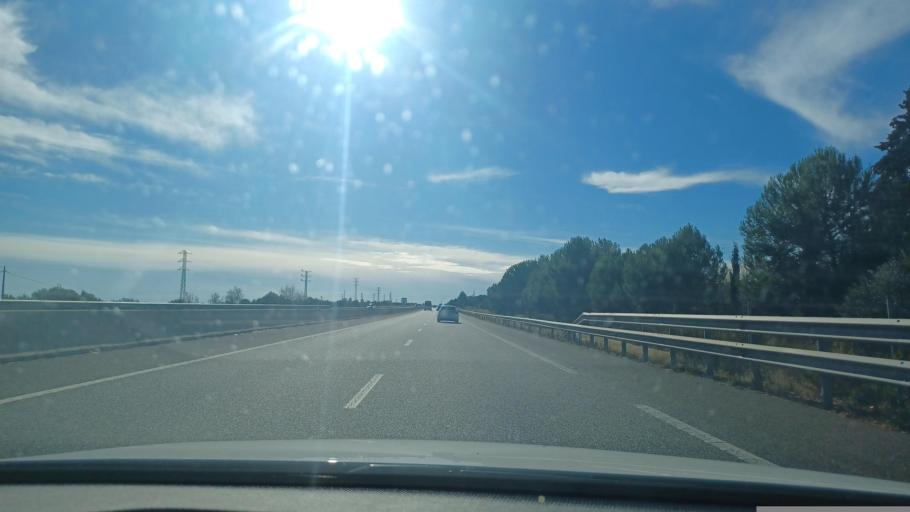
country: ES
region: Catalonia
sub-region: Provincia de Tarragona
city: Alcover
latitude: 41.2401
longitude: 1.1668
